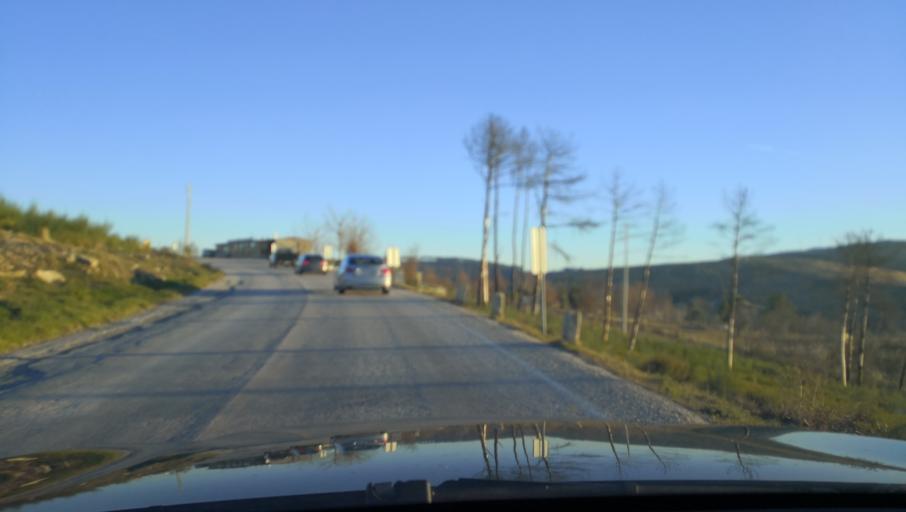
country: PT
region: Vila Real
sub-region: Ribeira de Pena
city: Ribeira de Pena
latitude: 41.4973
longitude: -7.7308
